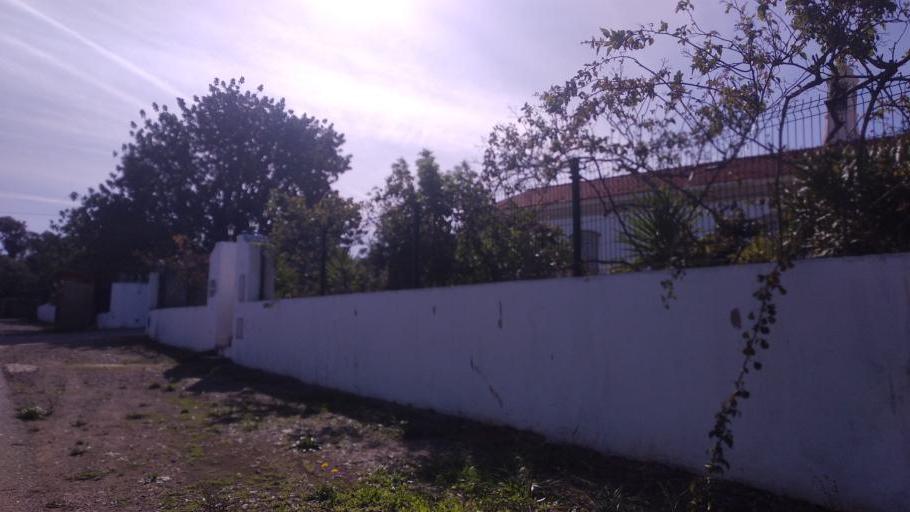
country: PT
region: Faro
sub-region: Sao Bras de Alportel
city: Sao Bras de Alportel
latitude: 37.1629
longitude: -7.9012
